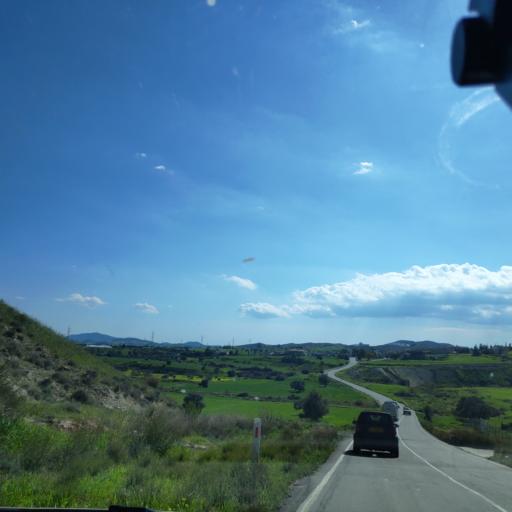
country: CY
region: Lefkosia
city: Tseri
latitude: 35.0296
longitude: 33.3277
